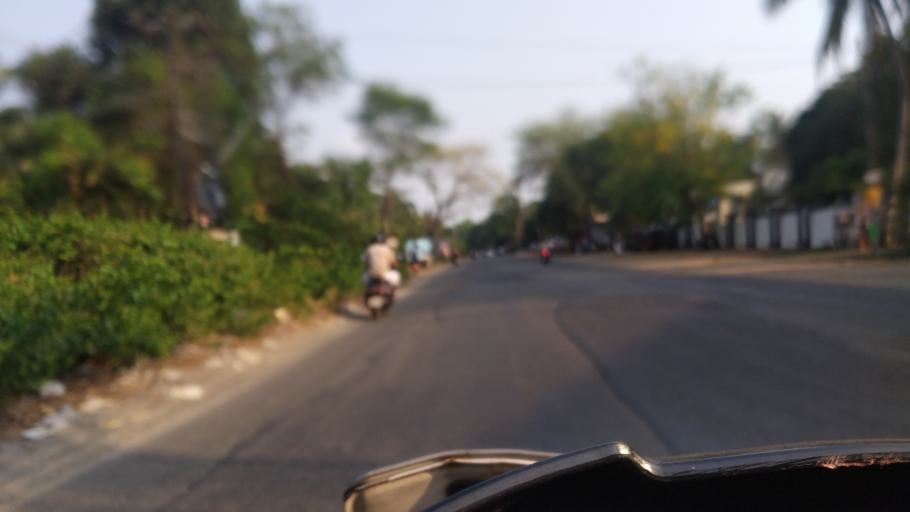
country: IN
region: Kerala
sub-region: Thrissur District
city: Thanniyam
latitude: 10.4364
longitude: 76.0975
